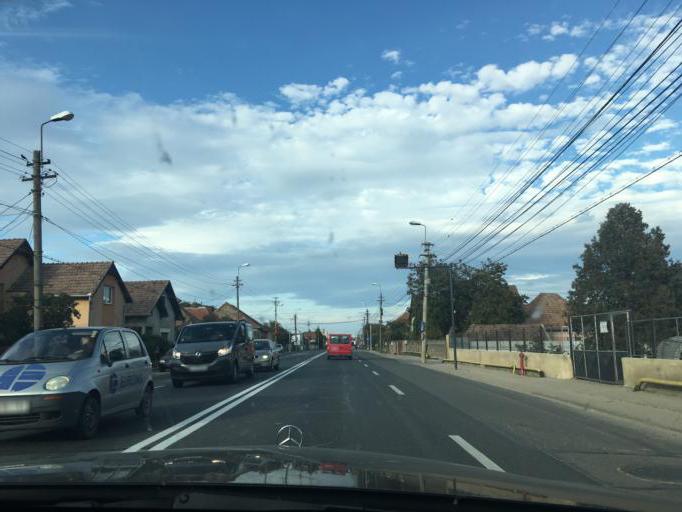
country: RO
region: Alba
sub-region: Municipiul Alba Iulia
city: Alba Iulia
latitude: 46.0449
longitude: 23.5651
